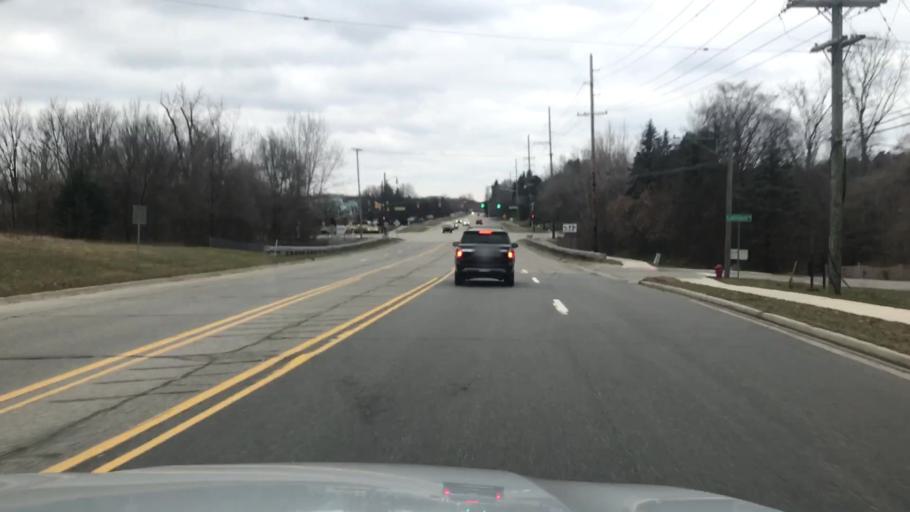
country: US
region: Michigan
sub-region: Wayne County
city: Northville
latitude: 42.4536
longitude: -83.4742
